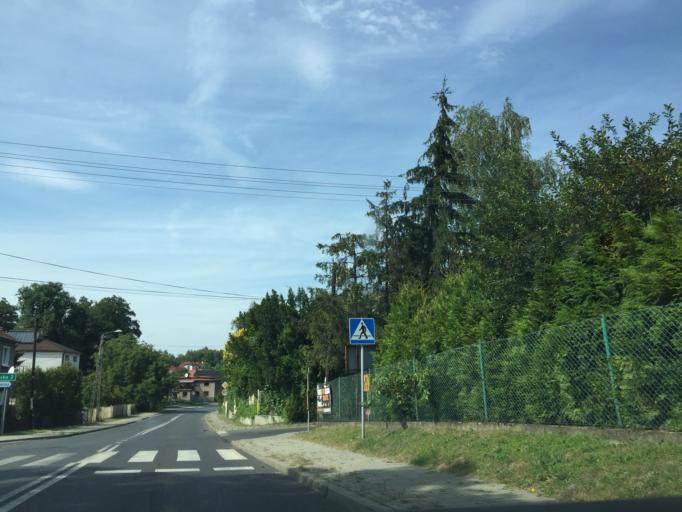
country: PL
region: Silesian Voivodeship
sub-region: Powiat wodzislawski
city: Gorzyce
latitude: 49.9563
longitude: 18.3997
